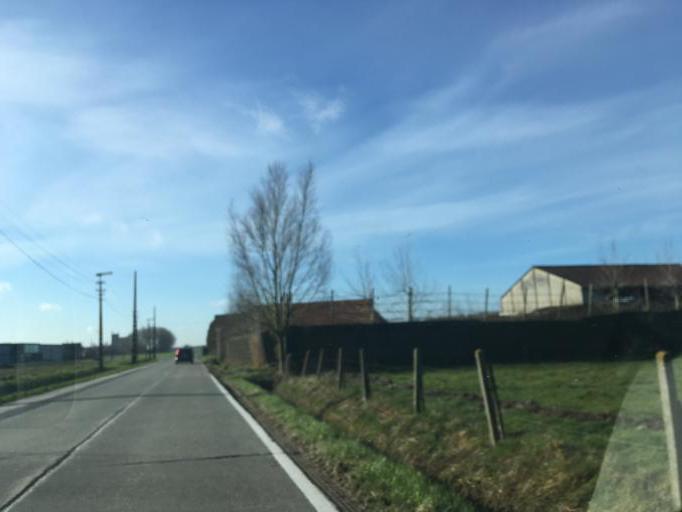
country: BE
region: Flanders
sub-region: Provincie West-Vlaanderen
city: Ledegem
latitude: 50.8857
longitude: 3.1480
